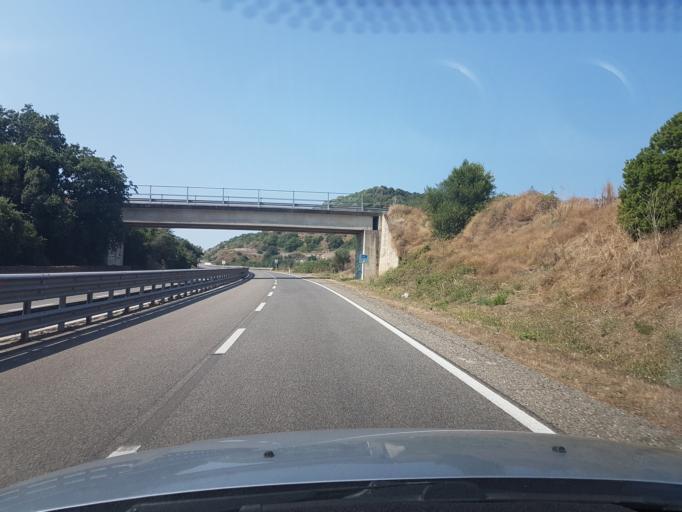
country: IT
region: Sardinia
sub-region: Provincia di Oristano
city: Soddi
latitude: 40.1435
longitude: 8.8742
